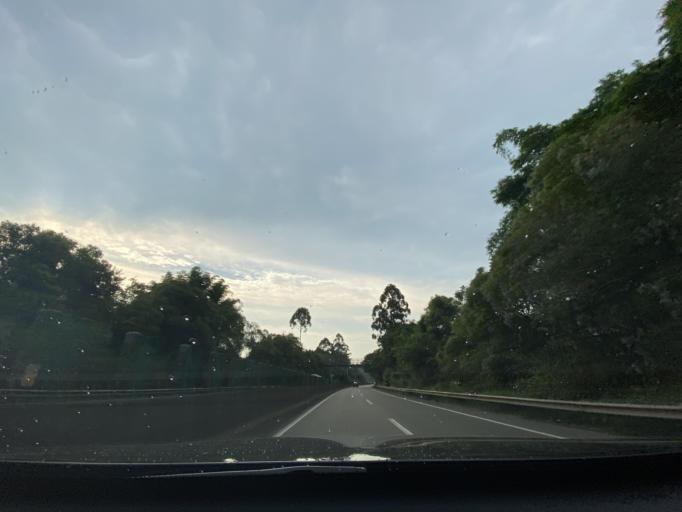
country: CN
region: Sichuan
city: Chonglong
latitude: 29.7913
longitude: 104.7267
